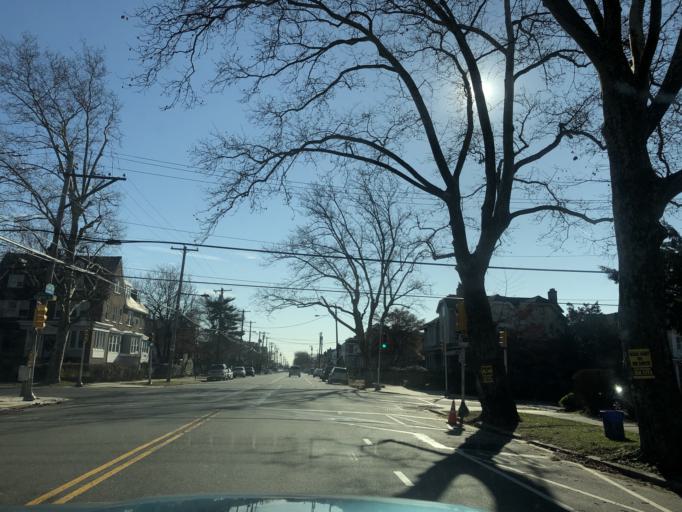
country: US
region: Pennsylvania
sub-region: Montgomery County
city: Bala-Cynwyd
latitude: 39.9893
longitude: -75.2331
